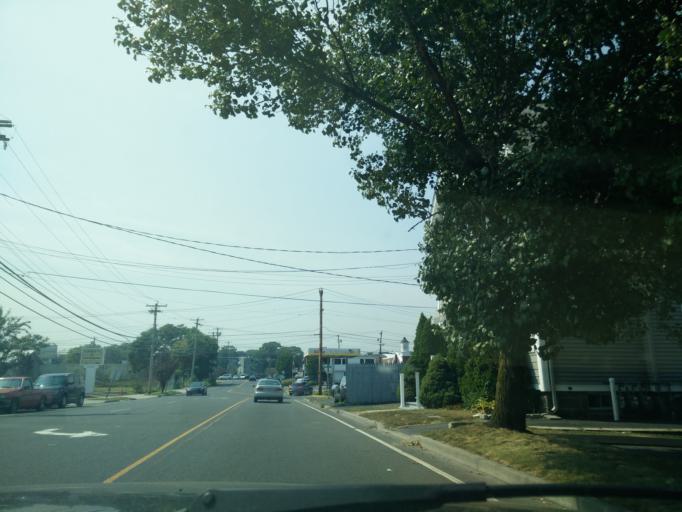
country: US
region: Connecticut
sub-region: Fairfield County
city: Bridgeport
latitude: 41.1647
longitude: -73.2315
